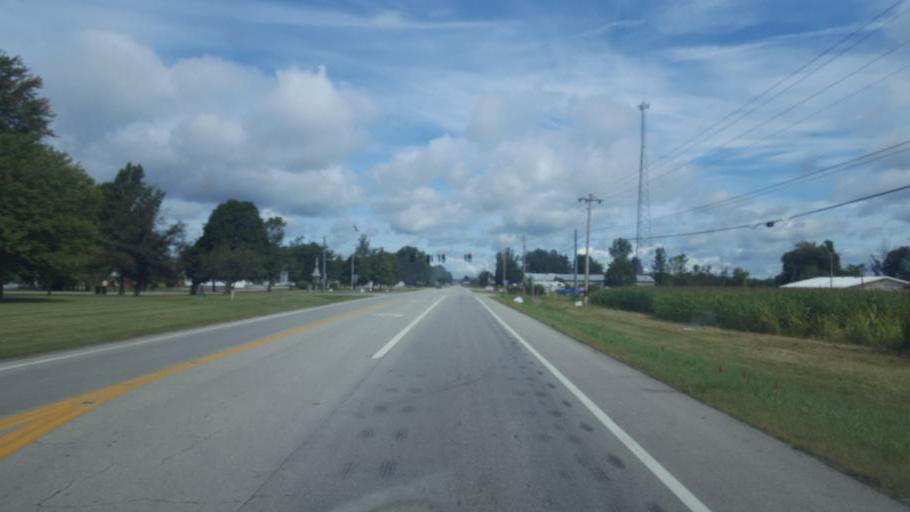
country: US
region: Ohio
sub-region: Lorain County
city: Oberlin
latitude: 41.2359
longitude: -82.2184
